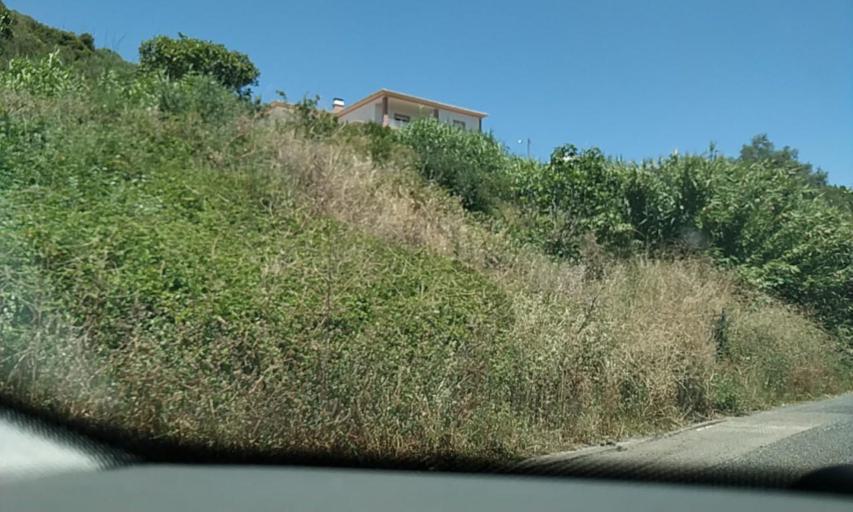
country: PT
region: Lisbon
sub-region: Odivelas
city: Canecas
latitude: 38.8665
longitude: -9.2160
